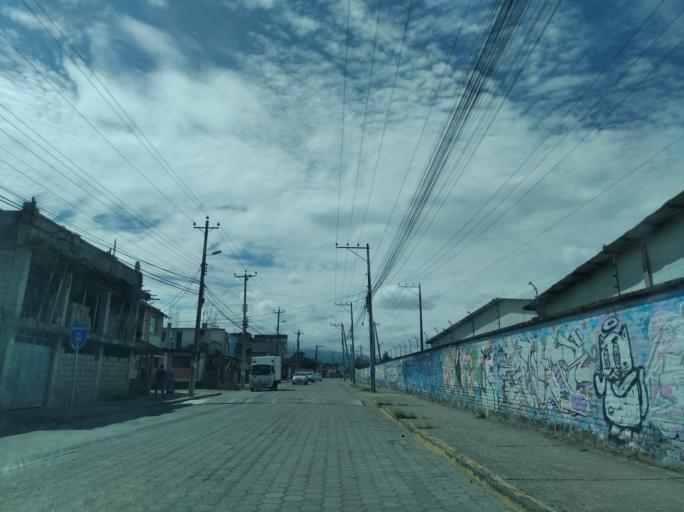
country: EC
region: Pichincha
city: Sangolqui
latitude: -0.2136
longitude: -78.3400
